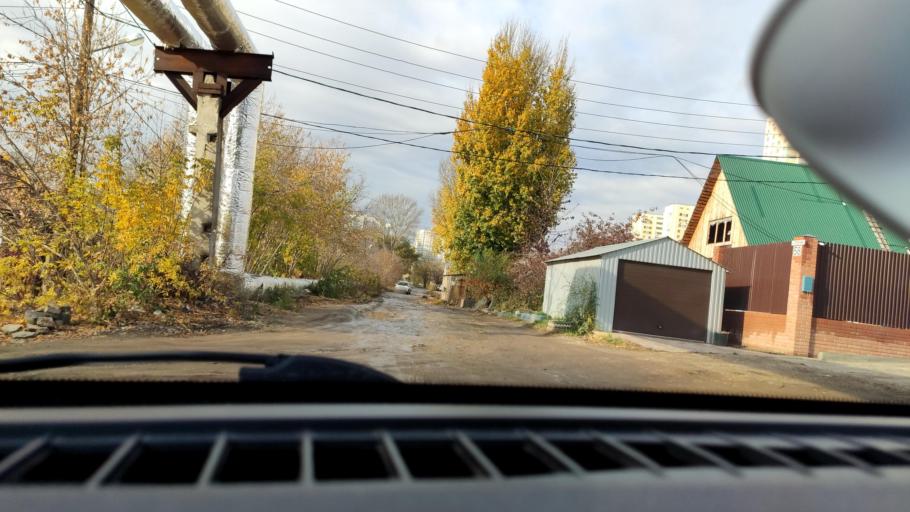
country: RU
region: Samara
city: Samara
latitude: 53.2041
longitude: 50.1962
